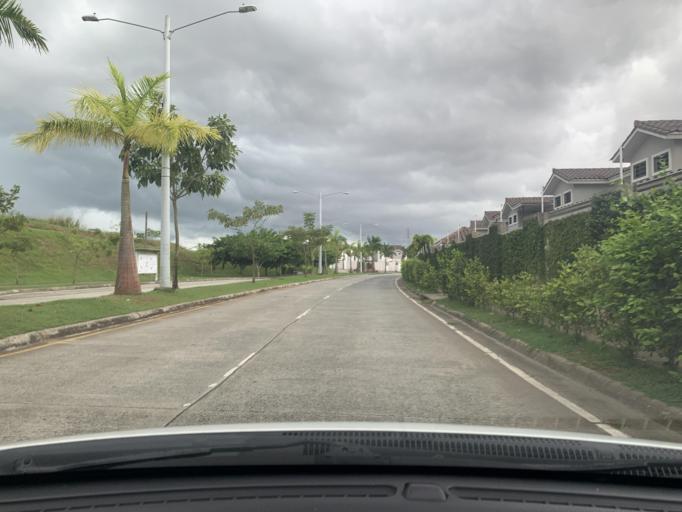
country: PA
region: Panama
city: San Miguelito
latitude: 9.0881
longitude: -79.4636
